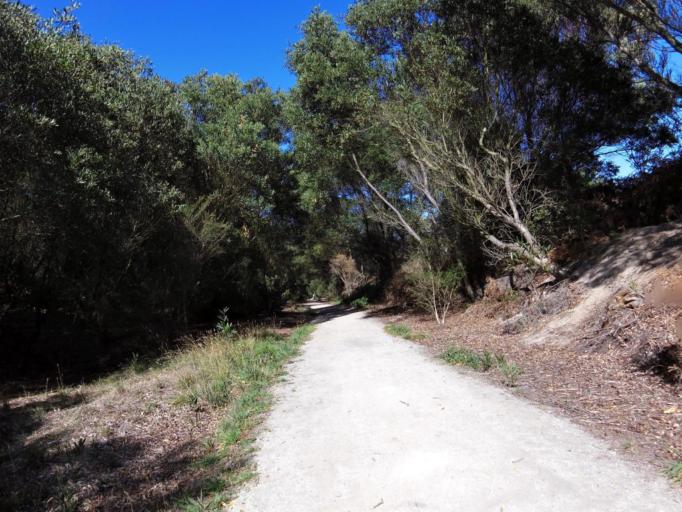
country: AU
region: Victoria
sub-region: Bass Coast
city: North Wonthaggi
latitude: -38.6129
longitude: 145.6010
